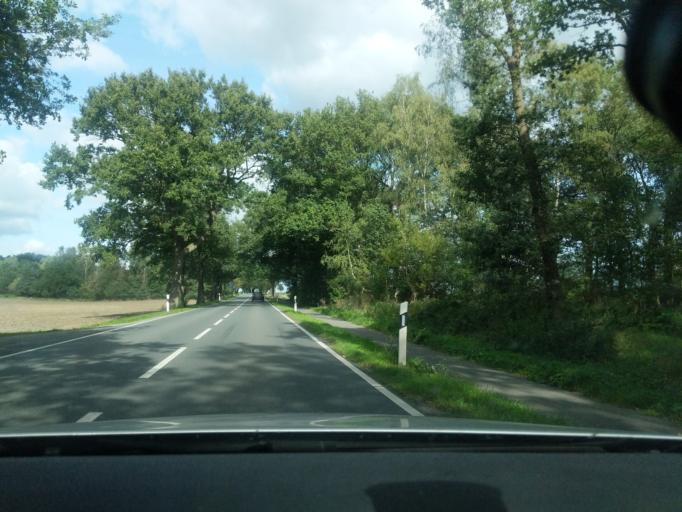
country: DE
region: Lower Saxony
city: Maasen
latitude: 52.6868
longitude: 8.8687
